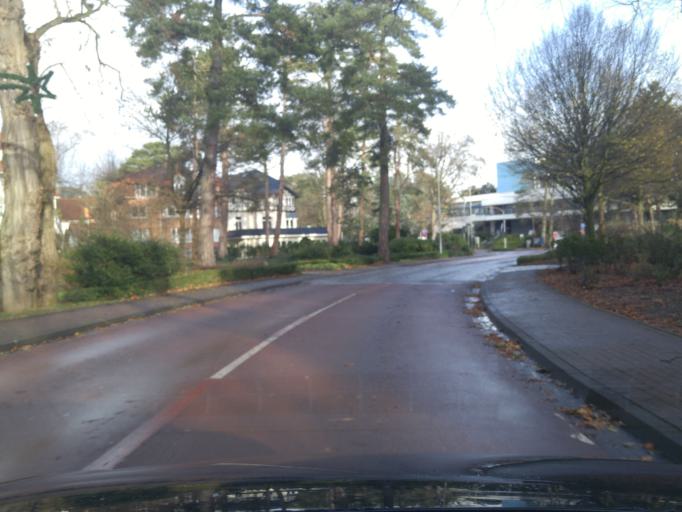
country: DE
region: Schleswig-Holstein
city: Timmendorfer Strand
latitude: 53.9999
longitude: 10.7787
